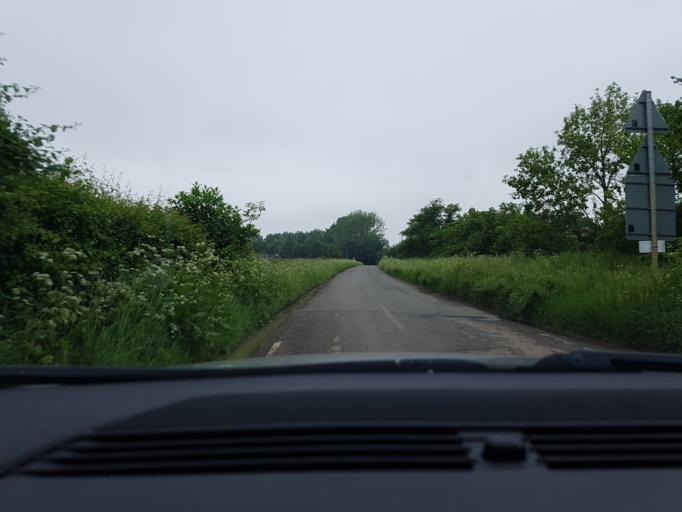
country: GB
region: England
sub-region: Buckinghamshire
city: Winslow
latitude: 51.9444
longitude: -0.9053
